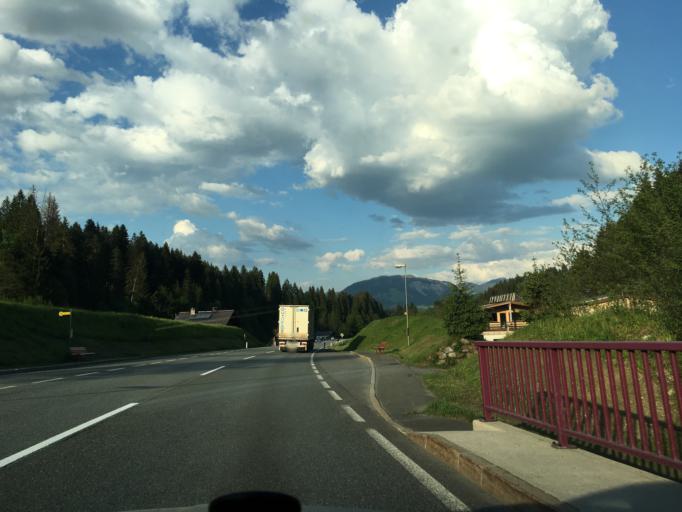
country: AT
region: Tyrol
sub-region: Politischer Bezirk Kitzbuhel
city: Oberndorf in Tirol
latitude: 47.5204
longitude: 12.3690
